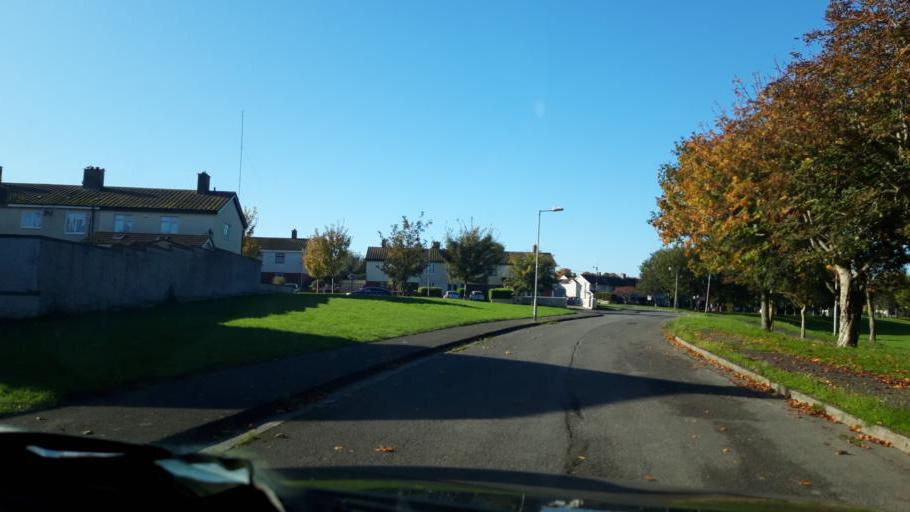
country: IE
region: Leinster
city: Raheny
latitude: 53.3811
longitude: -6.1819
